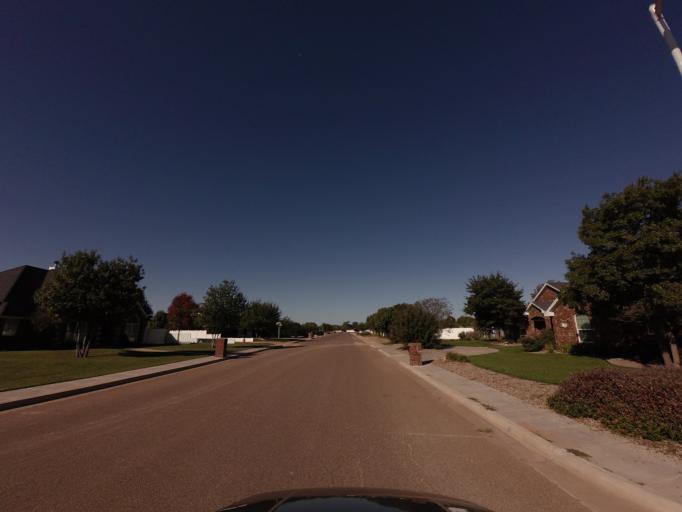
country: US
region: New Mexico
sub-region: Curry County
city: Clovis
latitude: 34.4392
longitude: -103.1745
